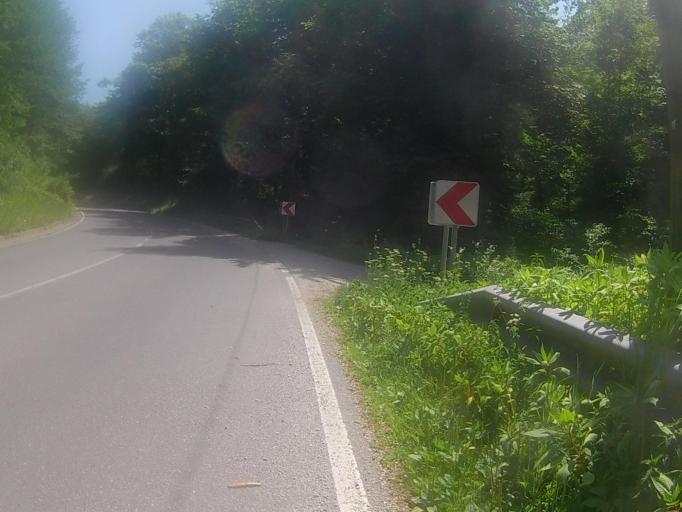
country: SI
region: Selnica ob Dravi
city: Selnica ob Dravi
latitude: 46.5417
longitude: 15.5008
